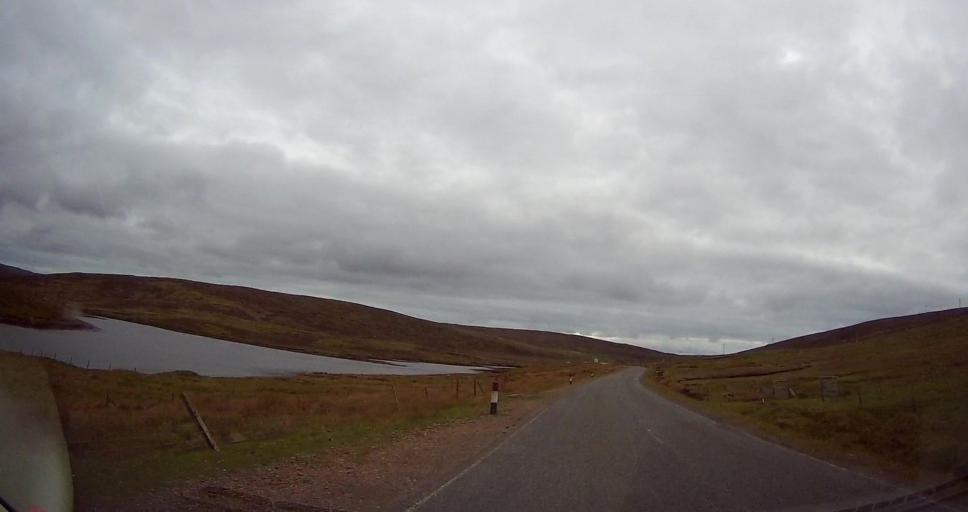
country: GB
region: Scotland
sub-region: Shetland Islands
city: Shetland
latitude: 60.6081
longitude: -1.0799
